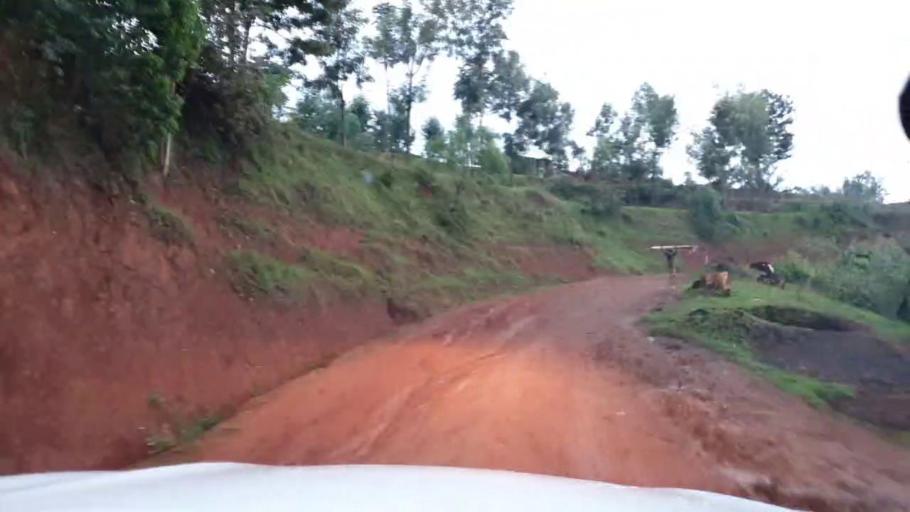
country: BI
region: Kayanza
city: Kayanza
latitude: -2.7142
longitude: 29.5406
